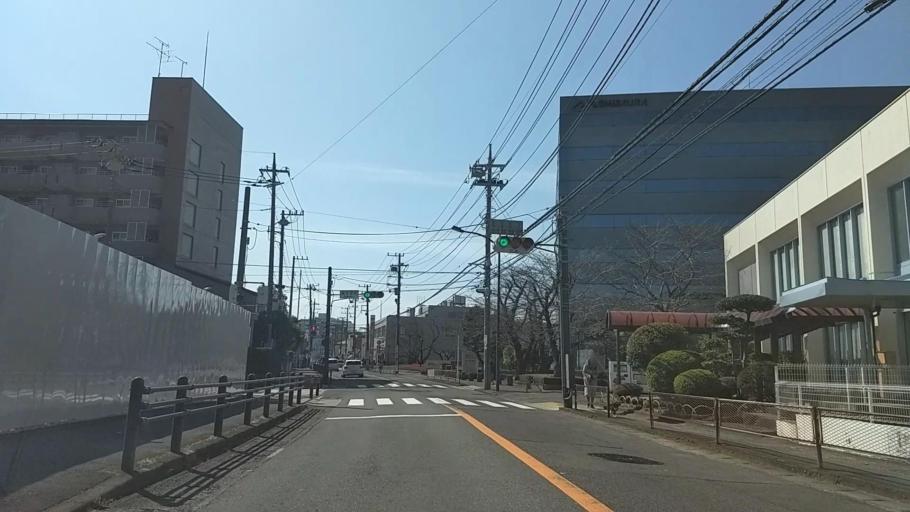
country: JP
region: Kanagawa
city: Kamakura
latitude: 35.3558
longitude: 139.5372
